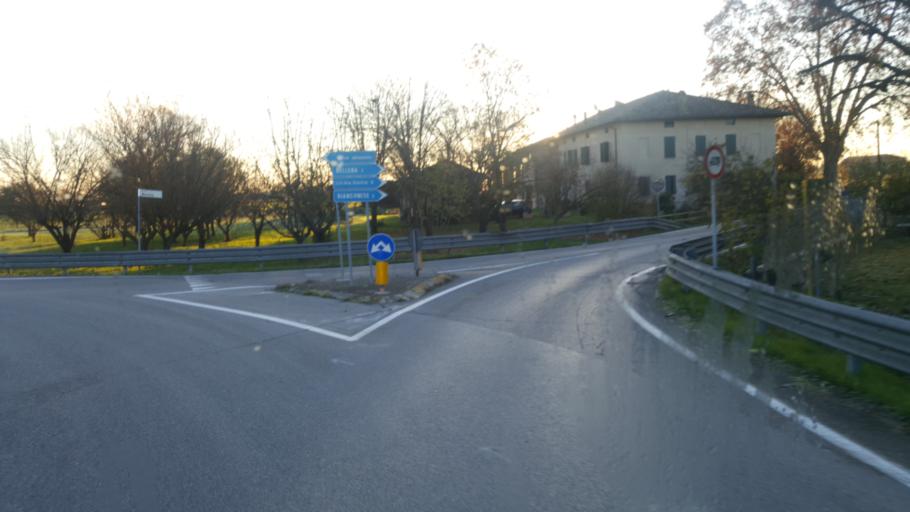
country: IT
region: Emilia-Romagna
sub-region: Provincia di Parma
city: Fontanellato
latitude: 44.8693
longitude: 10.1955
